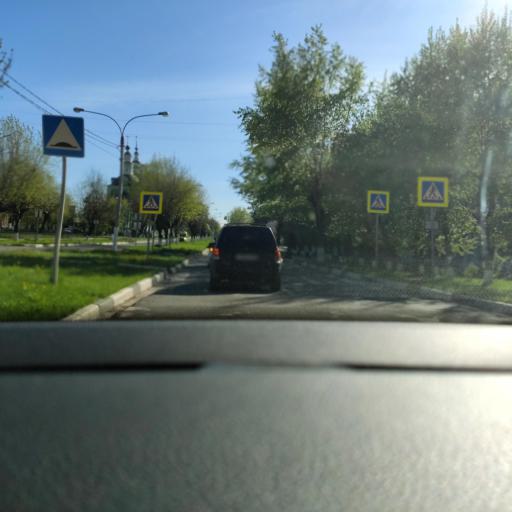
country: RU
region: Moskovskaya
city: Dmitrov
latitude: 56.3487
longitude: 37.5319
